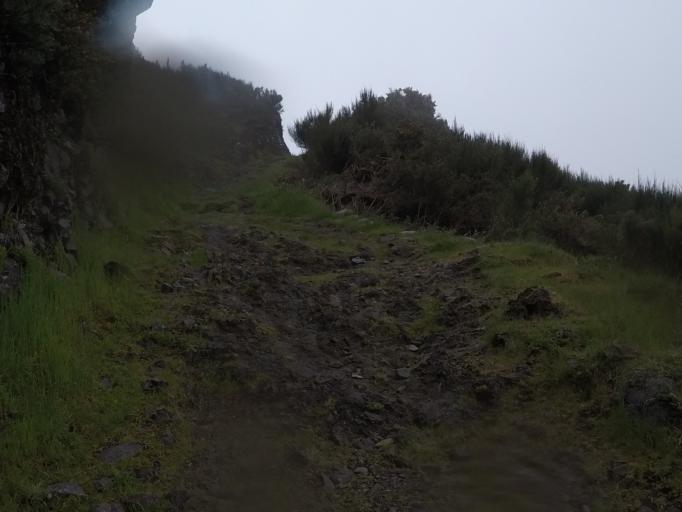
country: PT
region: Madeira
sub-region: Camara de Lobos
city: Curral das Freiras
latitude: 32.7282
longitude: -16.9851
